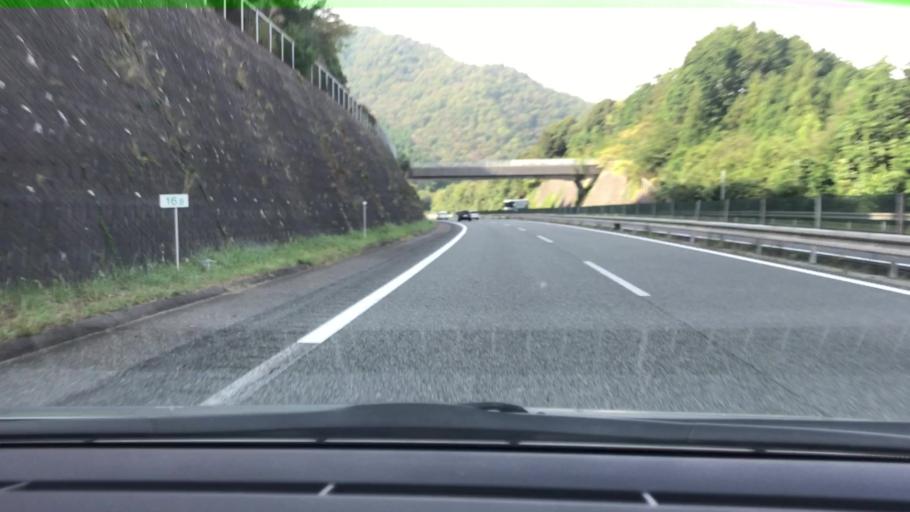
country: JP
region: Hyogo
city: Sasayama
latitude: 35.0185
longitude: 135.1745
